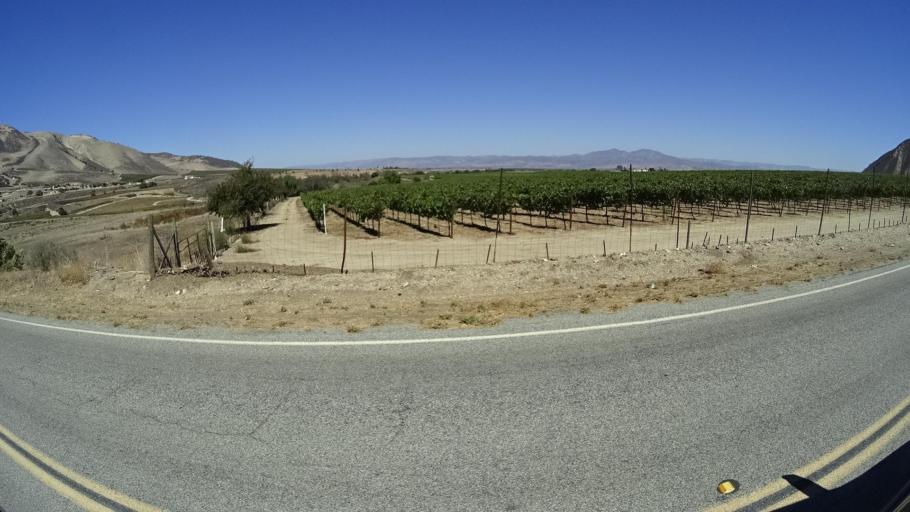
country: US
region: California
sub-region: Monterey County
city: Greenfield
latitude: 36.2787
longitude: -121.3134
